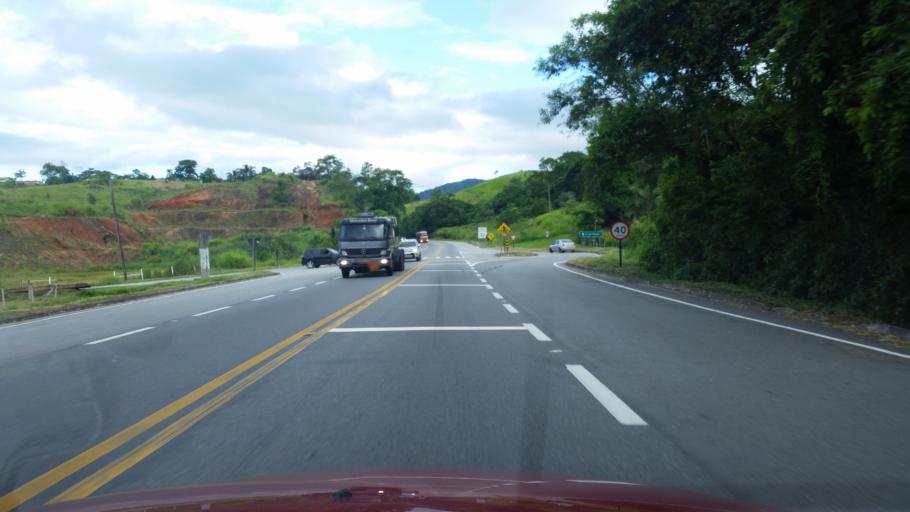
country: BR
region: Sao Paulo
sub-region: Miracatu
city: Miracatu
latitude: -24.2796
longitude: -47.2404
